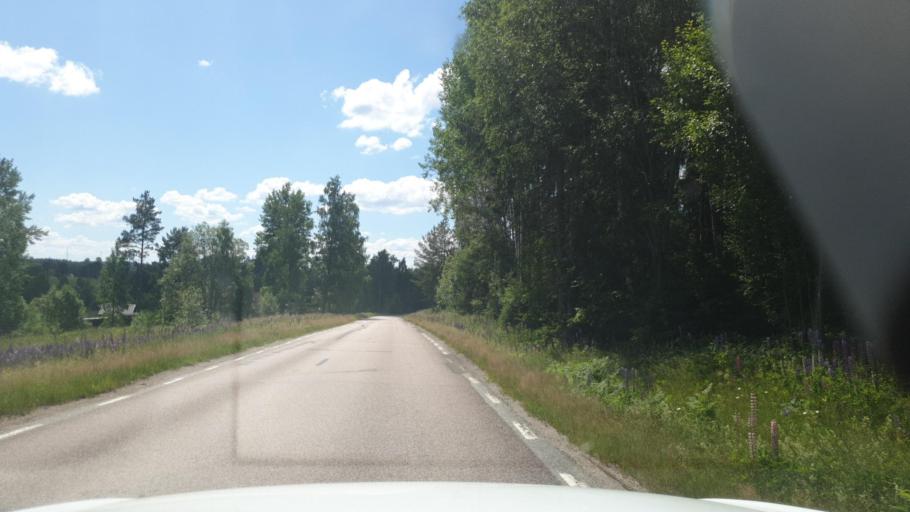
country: SE
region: Vaermland
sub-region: Arvika Kommun
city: Arvika
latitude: 59.6906
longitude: 12.7906
